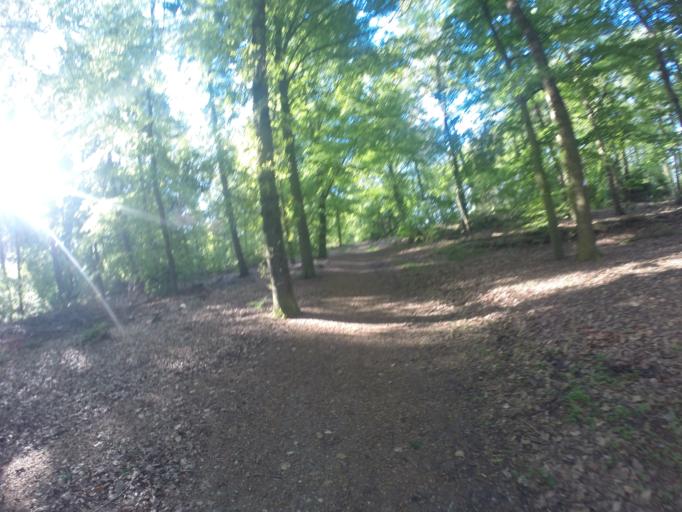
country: NL
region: Gelderland
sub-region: Gemeente Montferland
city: s-Heerenberg
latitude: 51.8857
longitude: 6.2375
